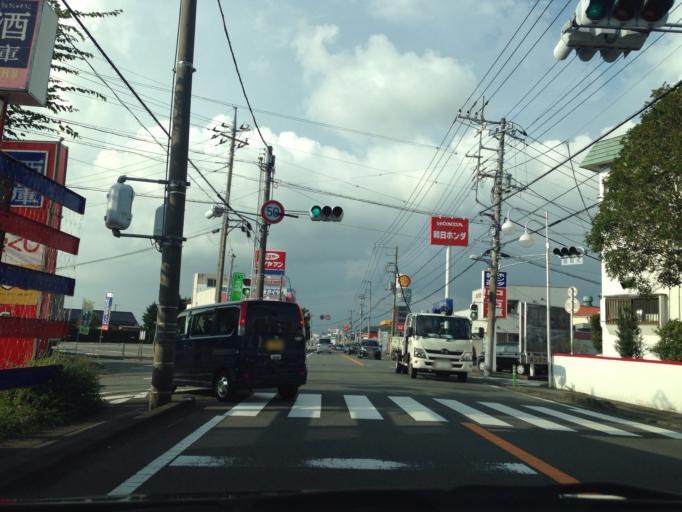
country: JP
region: Shizuoka
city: Mishima
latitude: 35.0187
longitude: 138.9452
